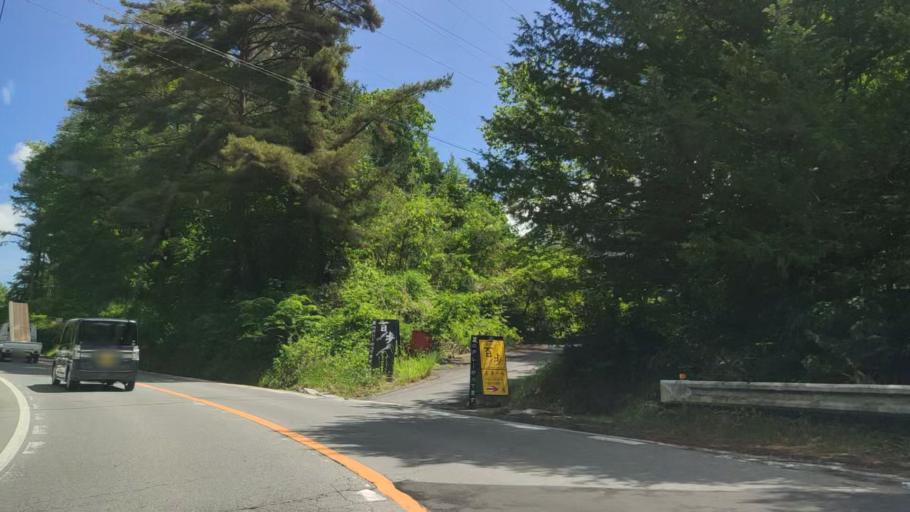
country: JP
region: Nagano
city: Chino
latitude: 36.0345
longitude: 138.2377
